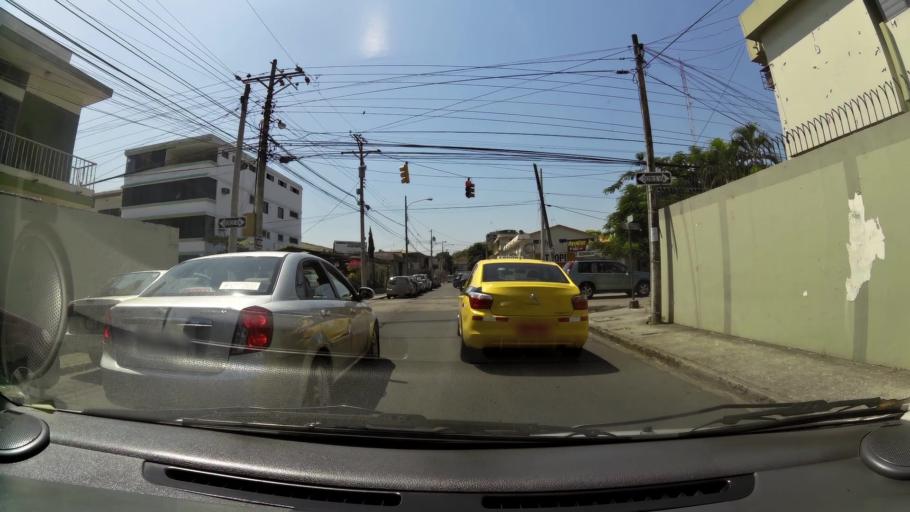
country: EC
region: Guayas
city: Guayaquil
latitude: -2.1656
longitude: -79.9139
